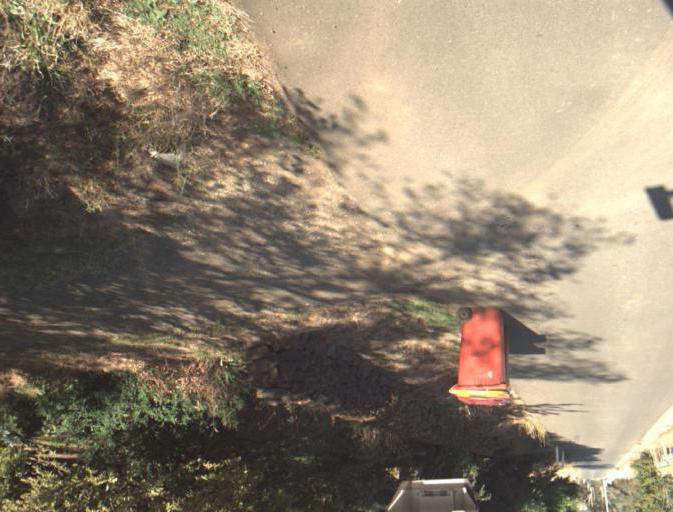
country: AU
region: Tasmania
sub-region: Launceston
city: Newstead
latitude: -41.4317
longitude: 147.2133
